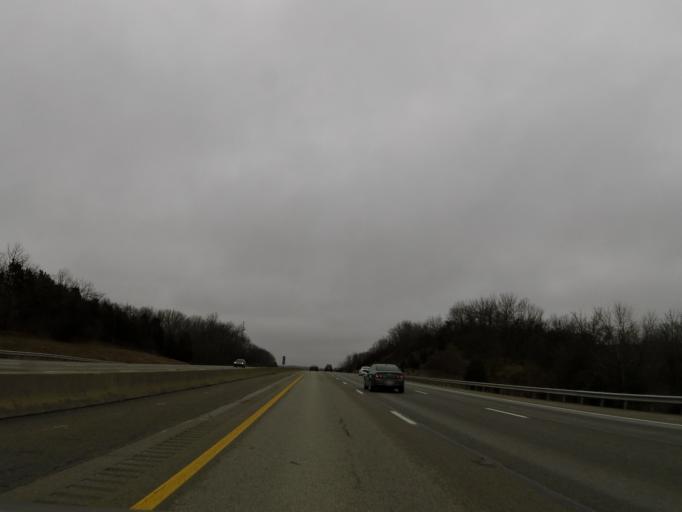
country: US
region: Kentucky
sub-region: Scott County
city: Georgetown
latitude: 38.3564
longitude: -84.5671
